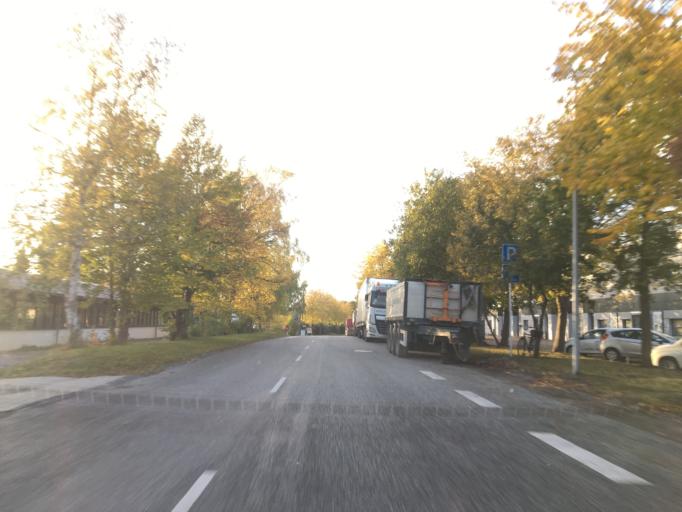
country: DK
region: Capital Region
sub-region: Allerod Kommune
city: Lillerod
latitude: 55.8828
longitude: 12.3505
